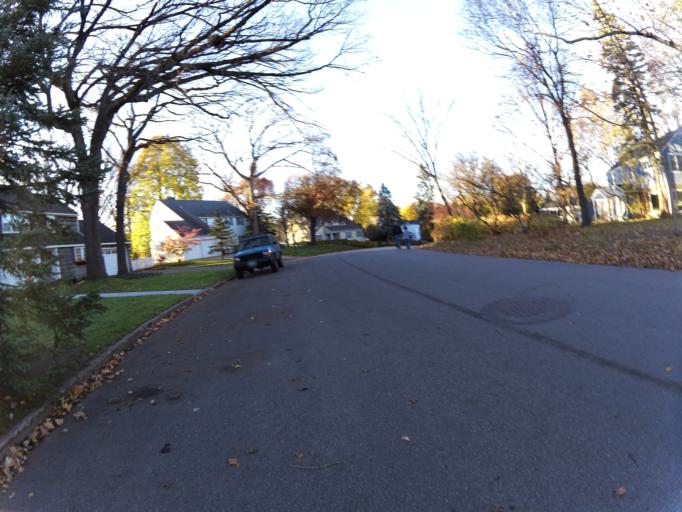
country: US
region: Minnesota
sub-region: Olmsted County
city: Rochester
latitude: 44.0128
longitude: -92.4821
